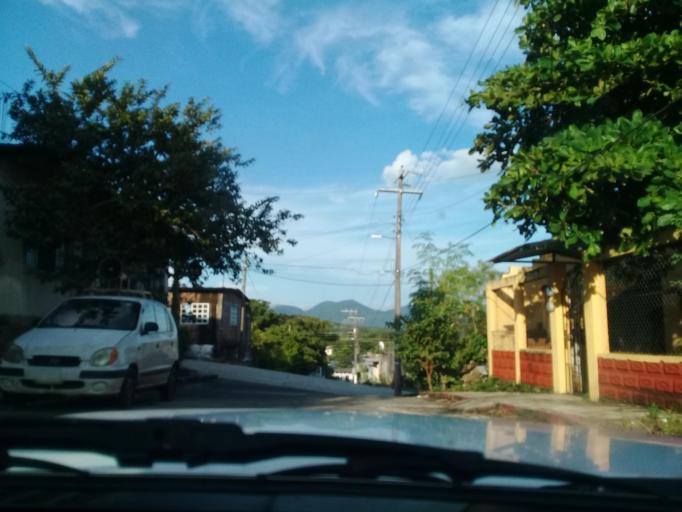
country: MX
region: Veracruz
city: Catemaco
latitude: 18.4227
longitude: -95.1001
